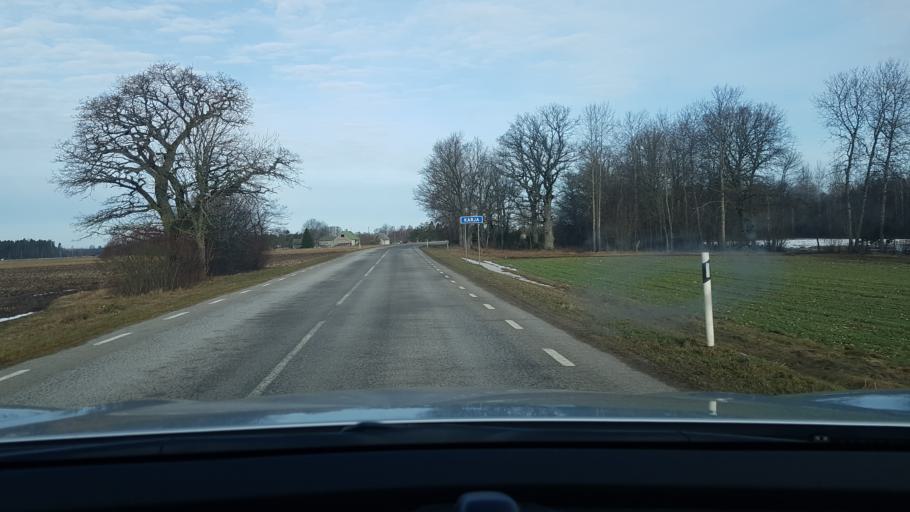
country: EE
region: Saare
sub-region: Kuressaare linn
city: Kuressaare
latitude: 58.4999
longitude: 22.7057
